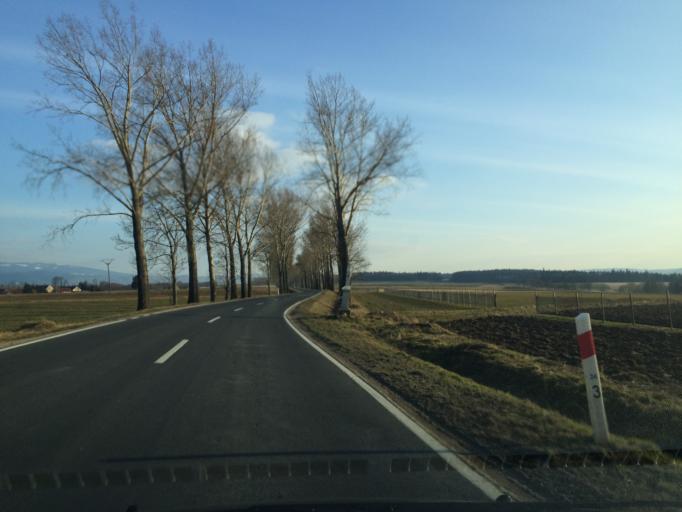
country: PL
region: Lower Silesian Voivodeship
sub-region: Powiat klodzki
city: Bystrzyca Klodzka
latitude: 50.2591
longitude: 16.6623
